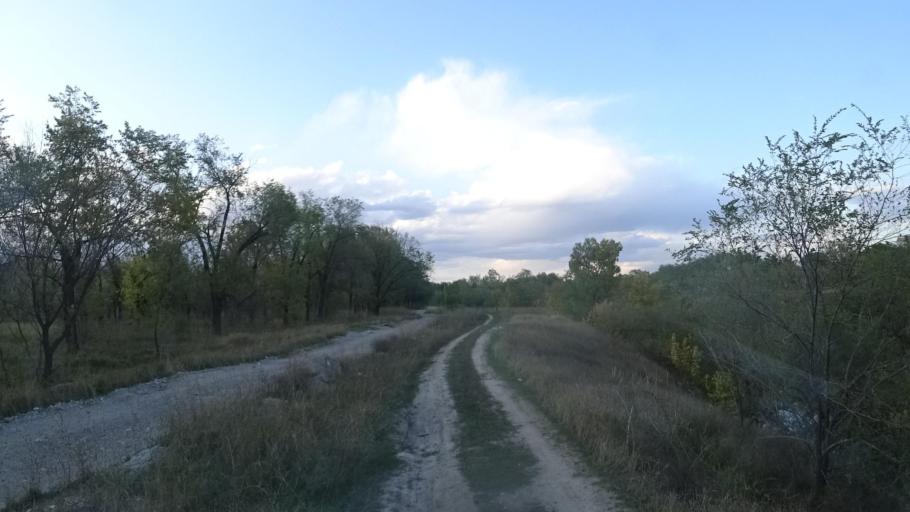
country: KZ
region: Almaty Oblysy
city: Pervomayskiy
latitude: 43.3342
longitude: 76.9995
